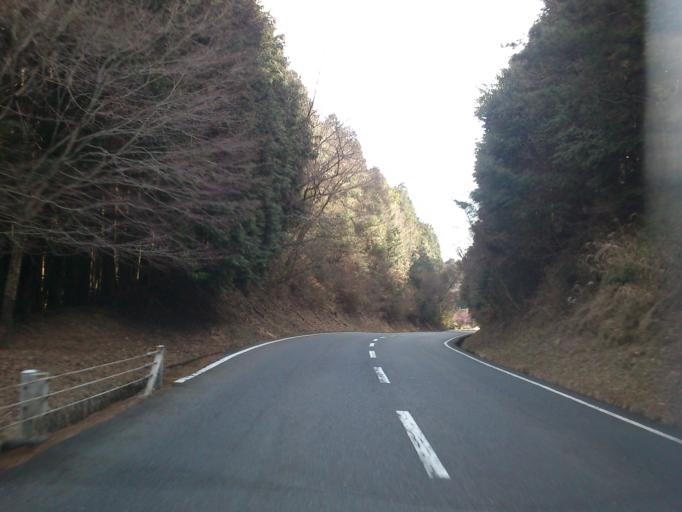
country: JP
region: Shiga Prefecture
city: Otsu-shi
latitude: 35.0427
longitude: 135.8388
